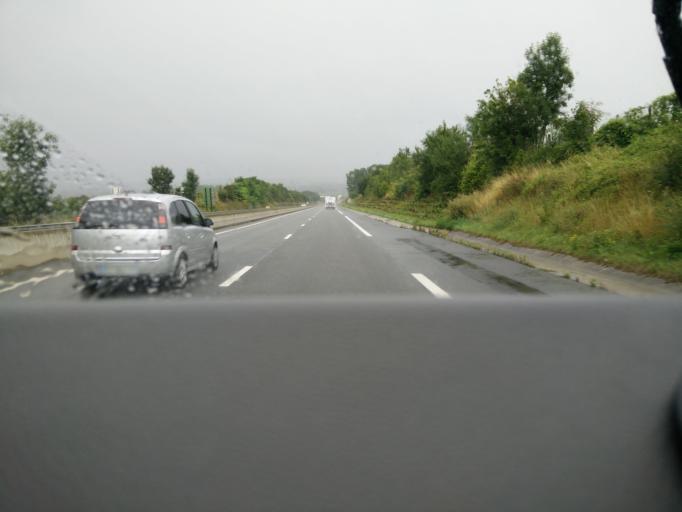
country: FR
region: Nord-Pas-de-Calais
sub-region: Departement du Pas-de-Calais
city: Marconnelle
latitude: 50.3625
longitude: 2.0102
